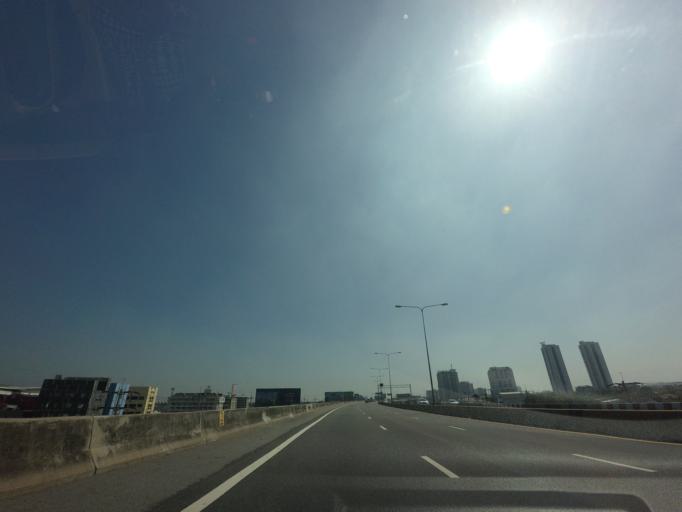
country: TH
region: Bangkok
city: Bang Na
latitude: 13.6636
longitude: 100.6572
